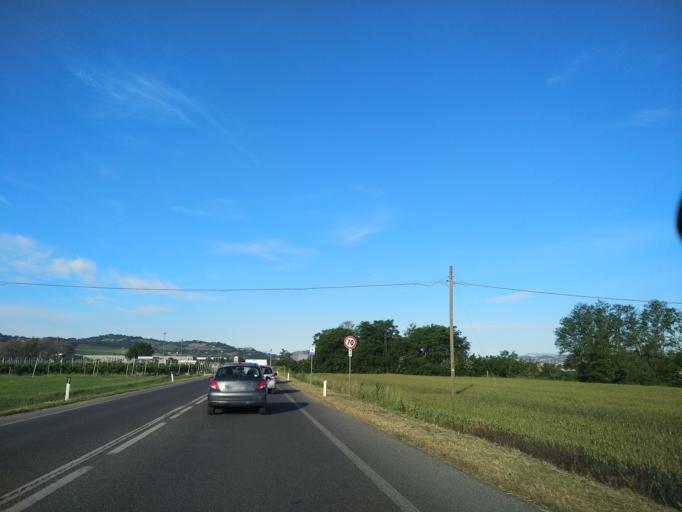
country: IT
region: The Marches
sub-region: Provincia di Pesaro e Urbino
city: Villa Ceccolini
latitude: 43.8690
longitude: 12.8312
